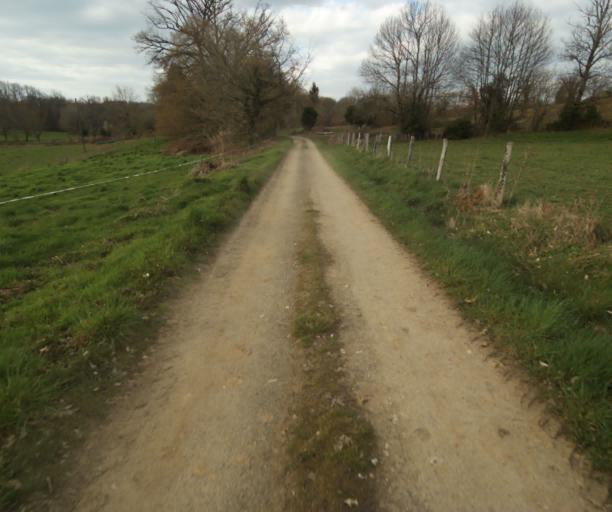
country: FR
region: Limousin
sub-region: Departement de la Correze
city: Saint-Clement
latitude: 45.3677
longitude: 1.6312
